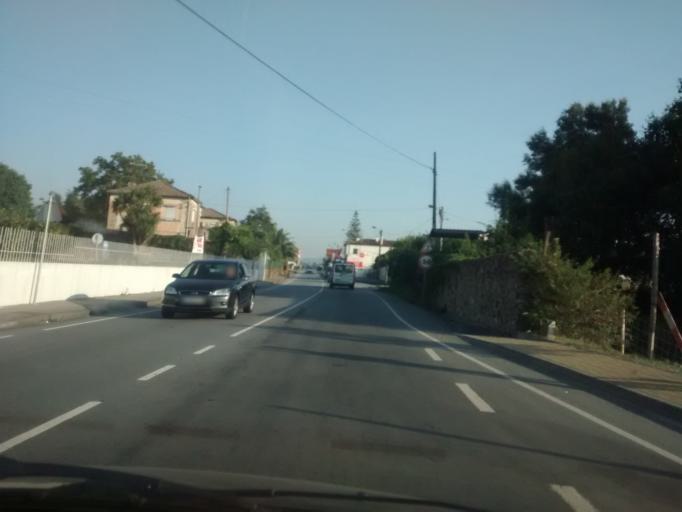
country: PT
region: Braga
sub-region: Braga
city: Braga
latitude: 41.5791
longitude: -8.4268
